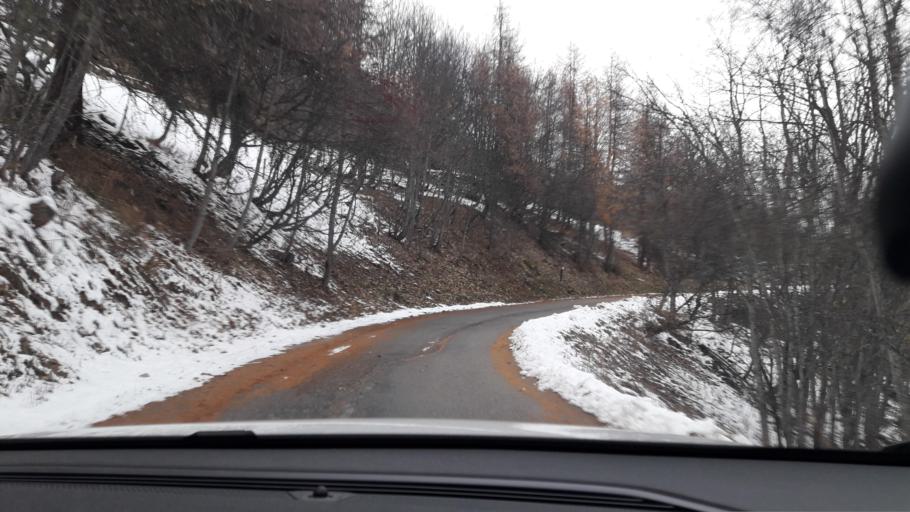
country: FR
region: Rhone-Alpes
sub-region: Departement de la Savoie
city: Valloire
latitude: 45.2002
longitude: 6.4168
